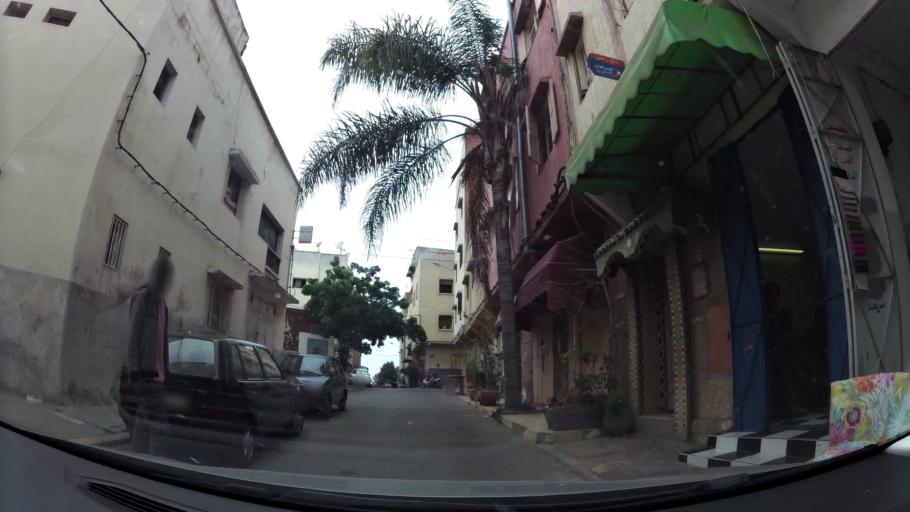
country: MA
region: Rabat-Sale-Zemmour-Zaer
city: Sale
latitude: 34.0289
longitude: -6.8053
